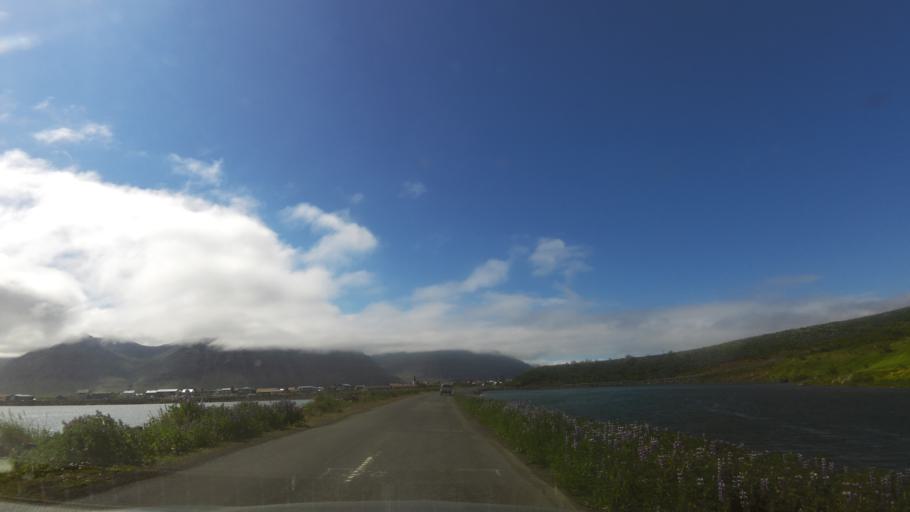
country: IS
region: Westfjords
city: Isafjoerdur
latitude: 66.0513
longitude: -23.5016
